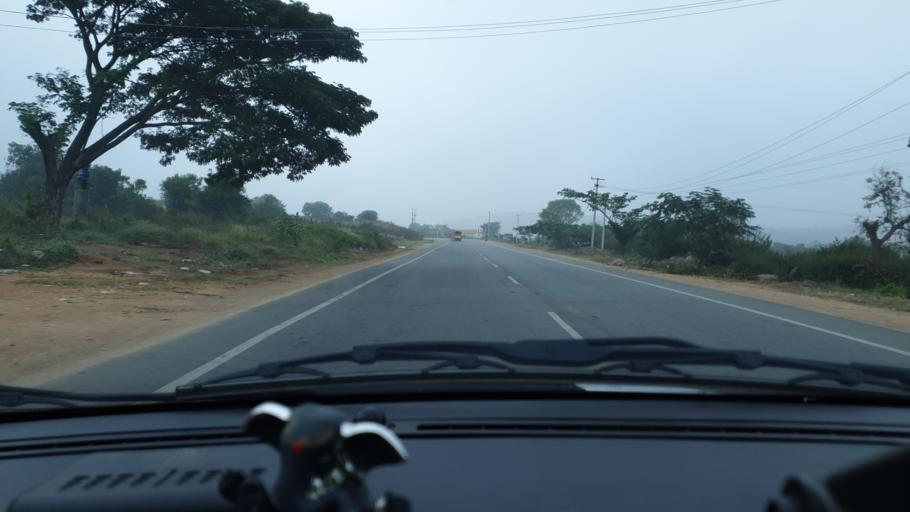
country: IN
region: Telangana
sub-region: Mahbubnagar
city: Farrukhnagar
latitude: 16.9591
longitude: 78.5129
